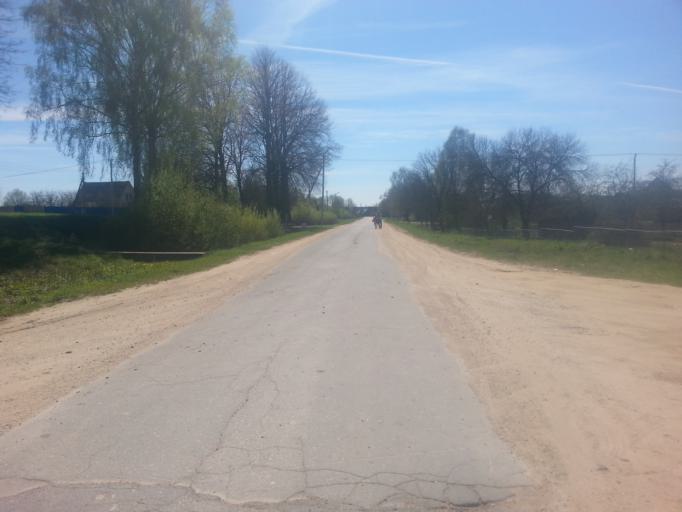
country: BY
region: Minsk
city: Narach
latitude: 54.9429
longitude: 26.6939
